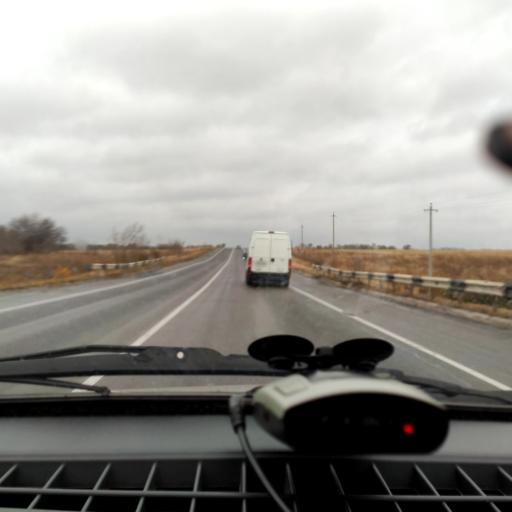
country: RU
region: Voronezj
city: Devitsa
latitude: 51.5726
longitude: 38.9747
